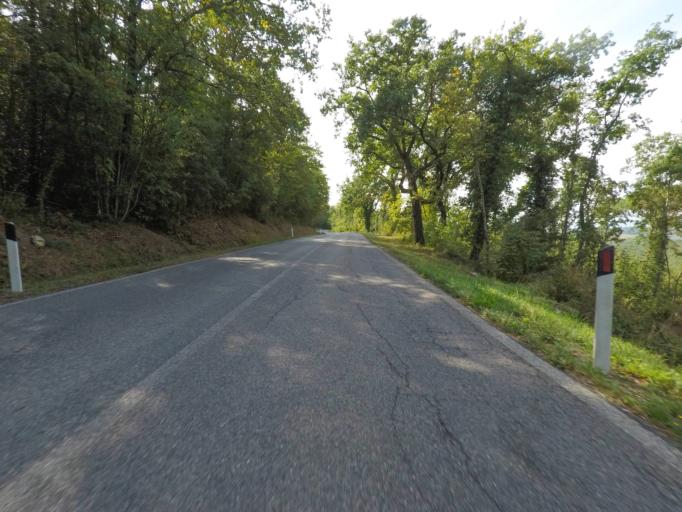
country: IT
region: Tuscany
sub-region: Provincia di Siena
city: Belverde
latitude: 43.3864
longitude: 11.3449
